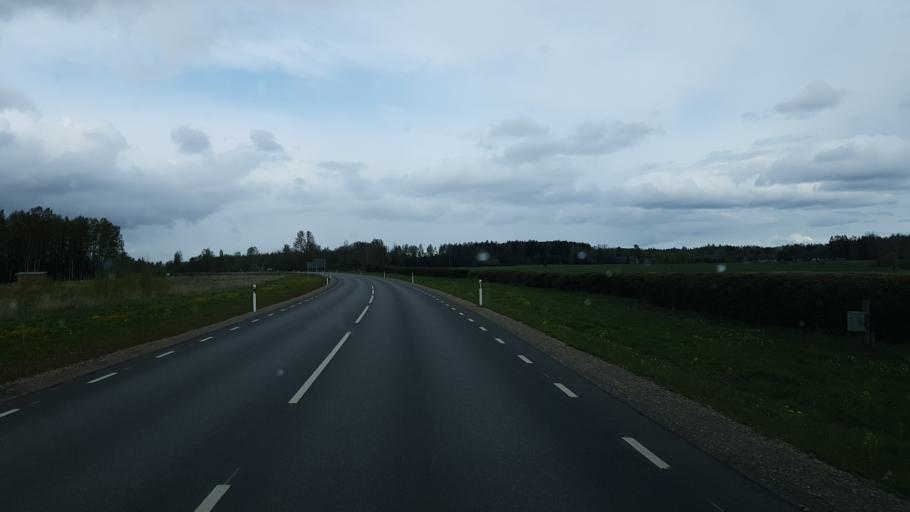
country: EE
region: Paernumaa
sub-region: Sindi linn
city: Sindi
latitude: 58.4496
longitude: 24.7725
